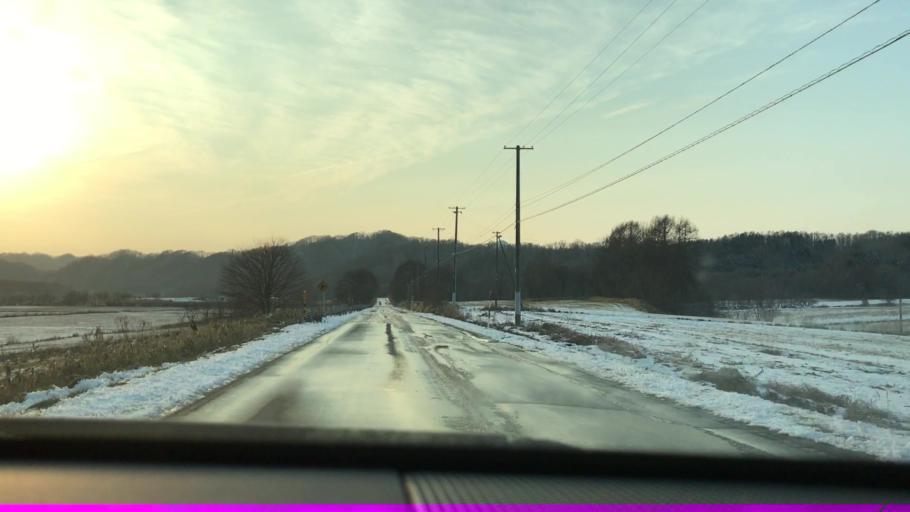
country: JP
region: Hokkaido
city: Shizunai-furukawacho
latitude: 42.5247
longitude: 142.3838
